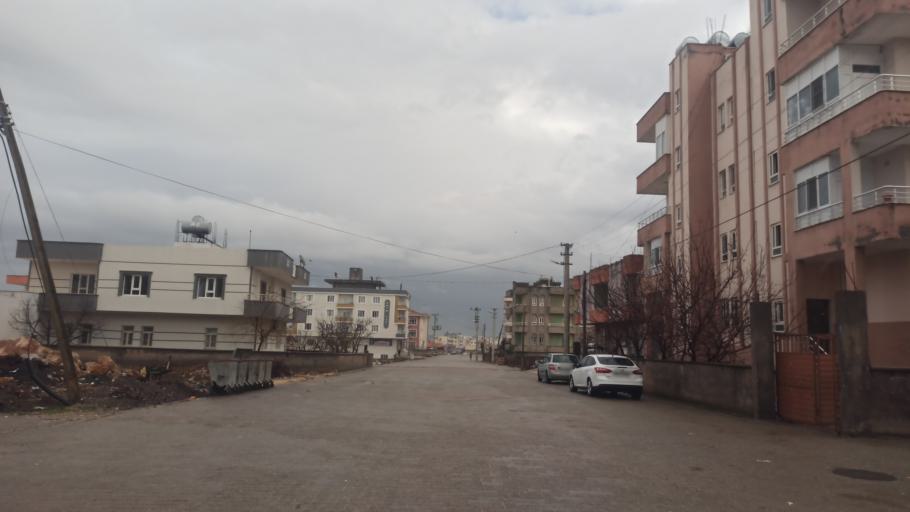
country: TR
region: Mardin
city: Midyat
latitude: 37.4232
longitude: 41.3554
